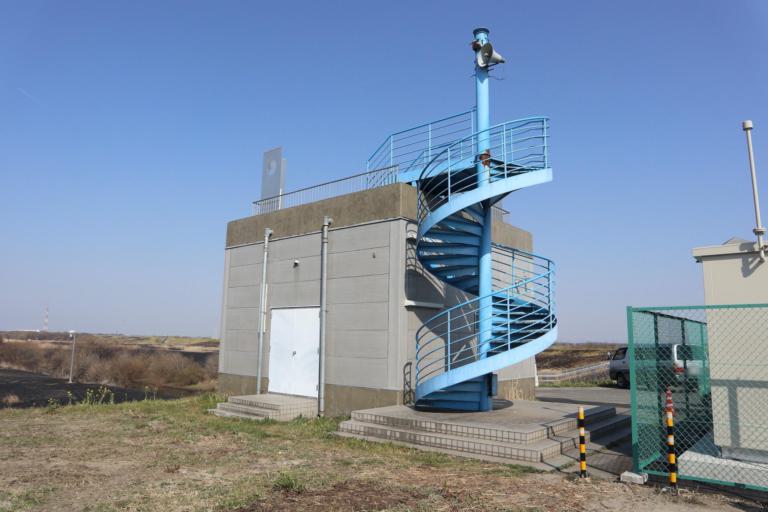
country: JP
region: Tochigi
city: Fujioka
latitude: 36.2547
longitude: 139.6812
